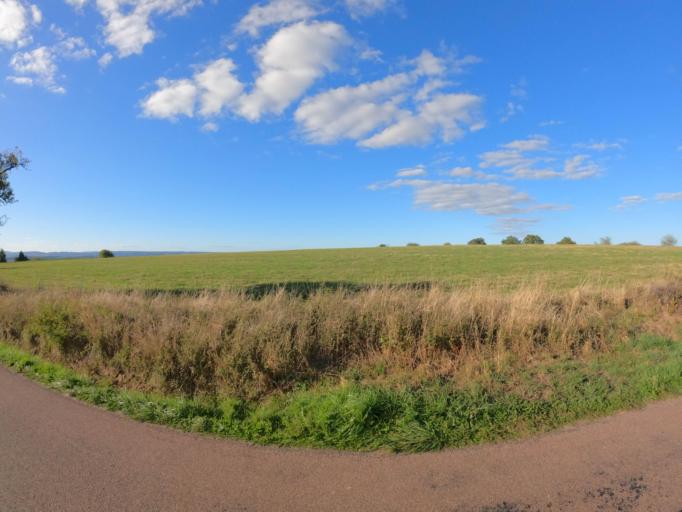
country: FR
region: Bourgogne
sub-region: Departement de Saone-et-Loire
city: Ecuisses
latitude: 46.7467
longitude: 4.5377
